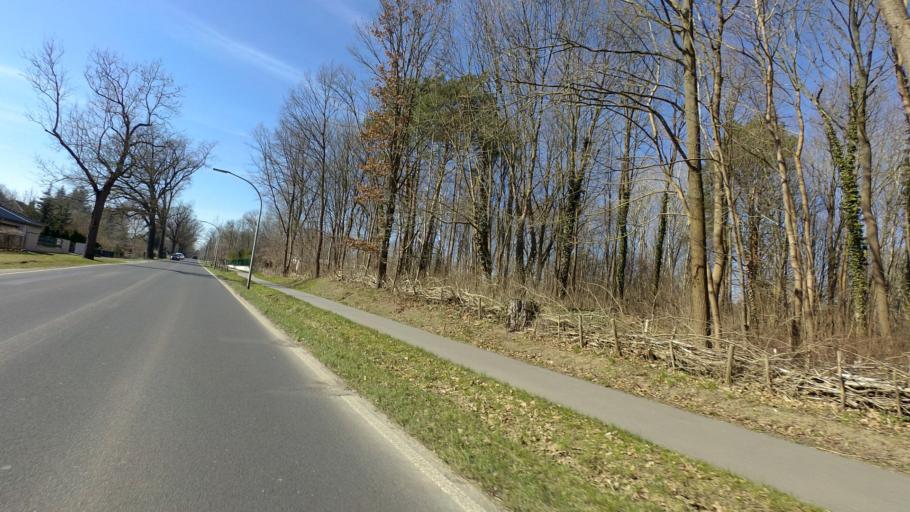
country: DE
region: Brandenburg
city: Muncheberg
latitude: 52.5222
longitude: 14.1042
